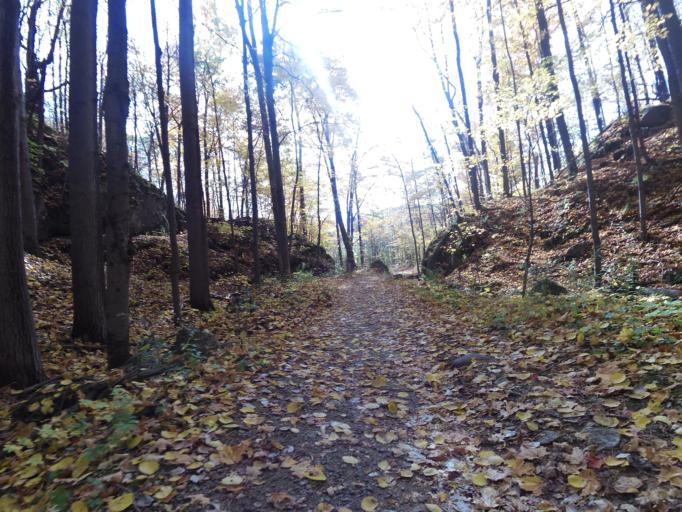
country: CA
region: Quebec
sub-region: Outaouais
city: Gatineau
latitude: 45.4716
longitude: -75.7960
